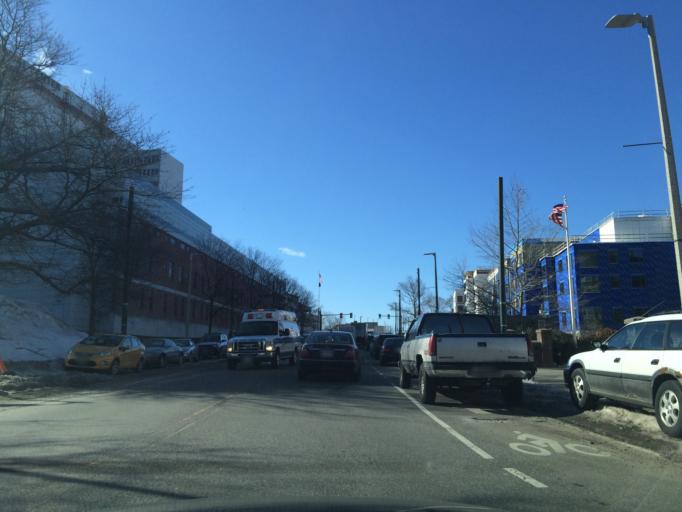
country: US
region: Massachusetts
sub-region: Norfolk County
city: Brookline
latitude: 42.3281
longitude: -71.1108
